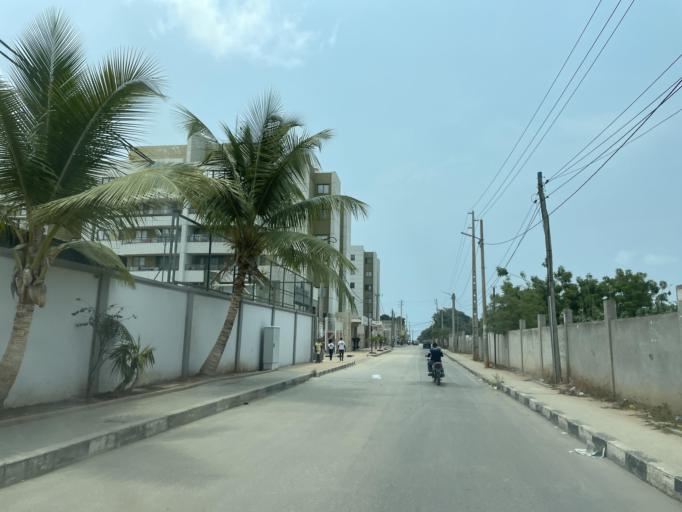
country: AO
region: Luanda
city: Luanda
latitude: -8.9416
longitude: 13.1654
